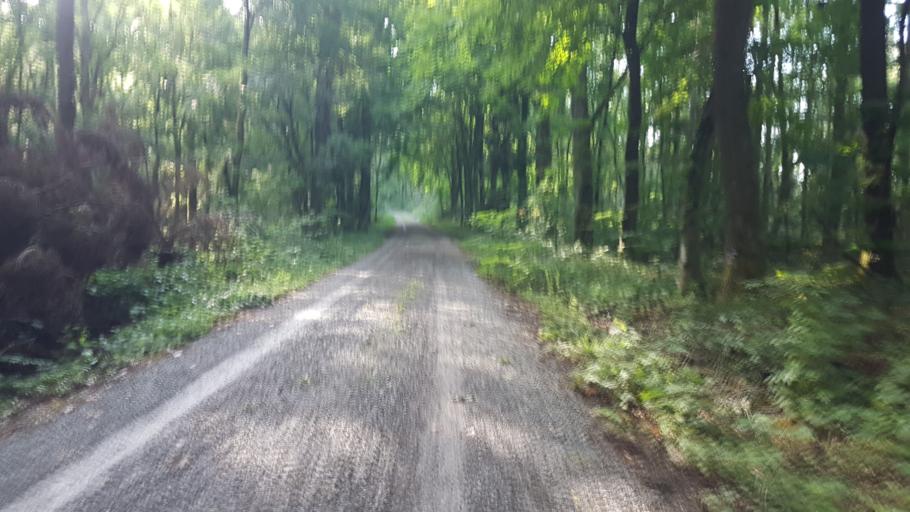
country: DE
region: Baden-Wuerttemberg
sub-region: Regierungsbezirk Stuttgart
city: Zaberfeld
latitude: 49.0424
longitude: 8.8987
